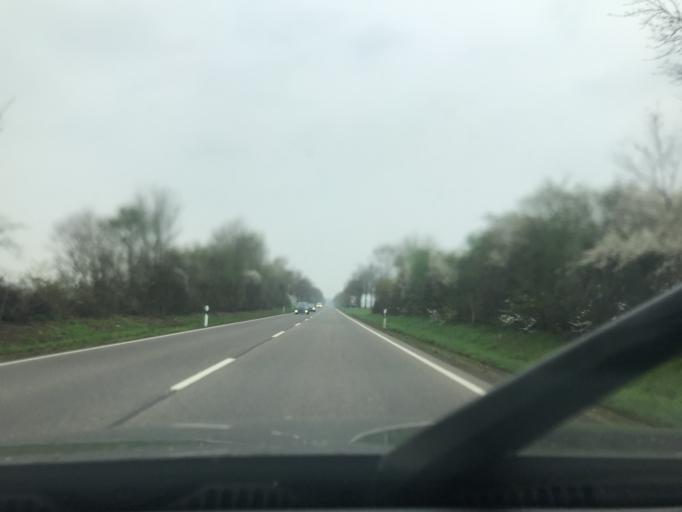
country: DE
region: North Rhine-Westphalia
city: Kempen
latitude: 51.3460
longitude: 6.4096
